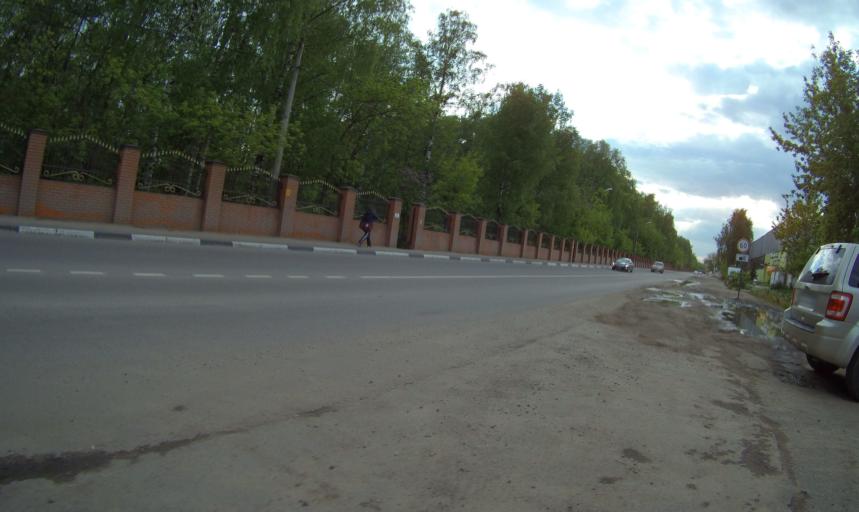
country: RU
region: Moskovskaya
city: Ramenskoye
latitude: 55.5687
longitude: 38.2579
